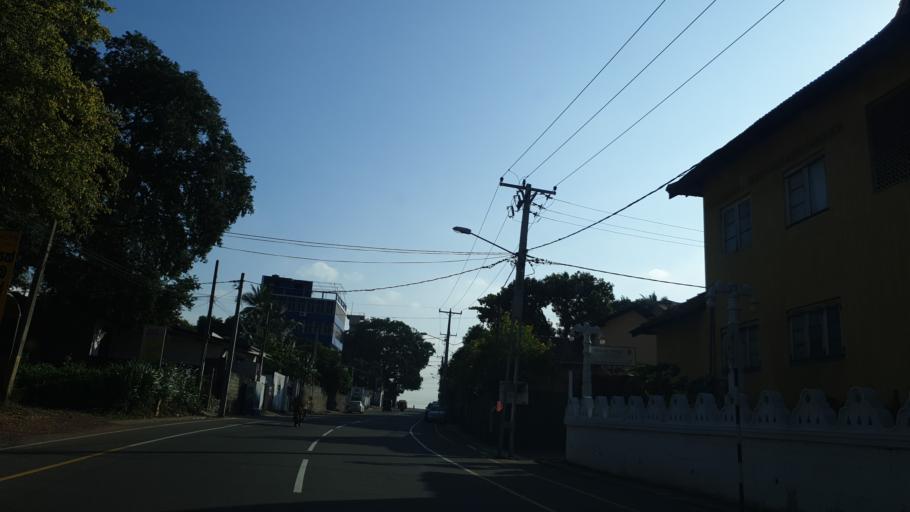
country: LK
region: Western
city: Sri Jayewardenepura Kotte
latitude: 6.8676
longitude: 79.8974
